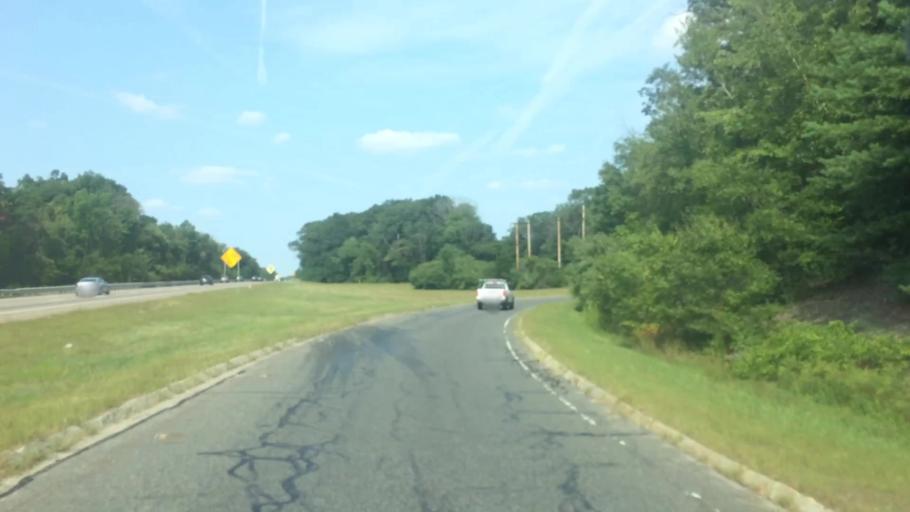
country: US
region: Massachusetts
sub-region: Bristol County
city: Attleboro
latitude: 41.9311
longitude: -71.3210
